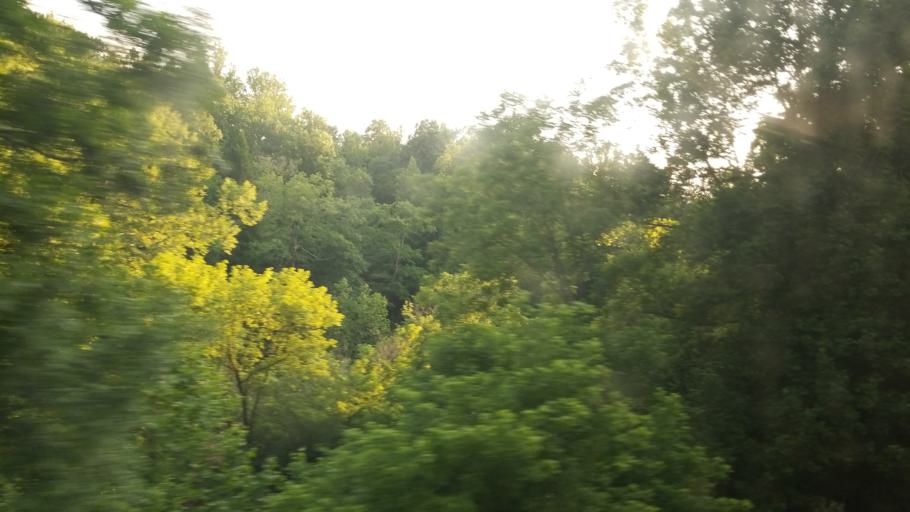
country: US
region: Virginia
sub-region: Prince William County
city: Yorkshire
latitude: 38.7761
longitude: -77.4202
